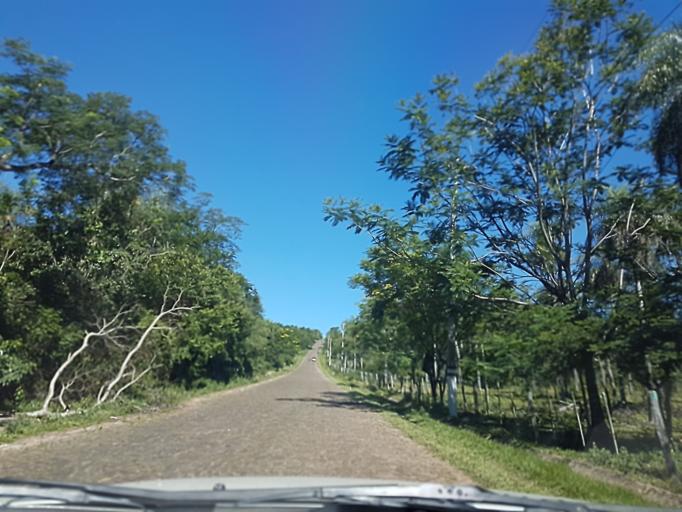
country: PY
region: Cordillera
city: Atyra
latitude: -25.2784
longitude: -57.1540
